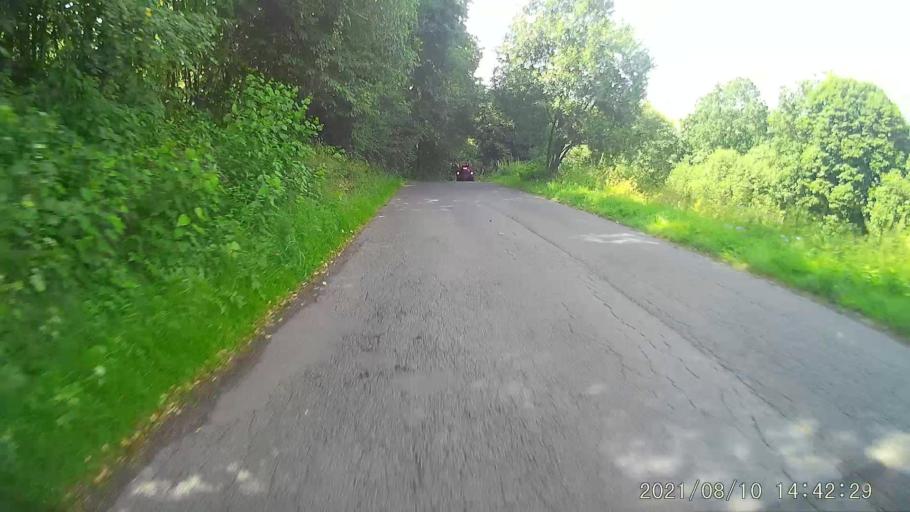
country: PL
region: Lower Silesian Voivodeship
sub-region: Powiat klodzki
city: Radkow
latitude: 50.5517
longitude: 16.4315
